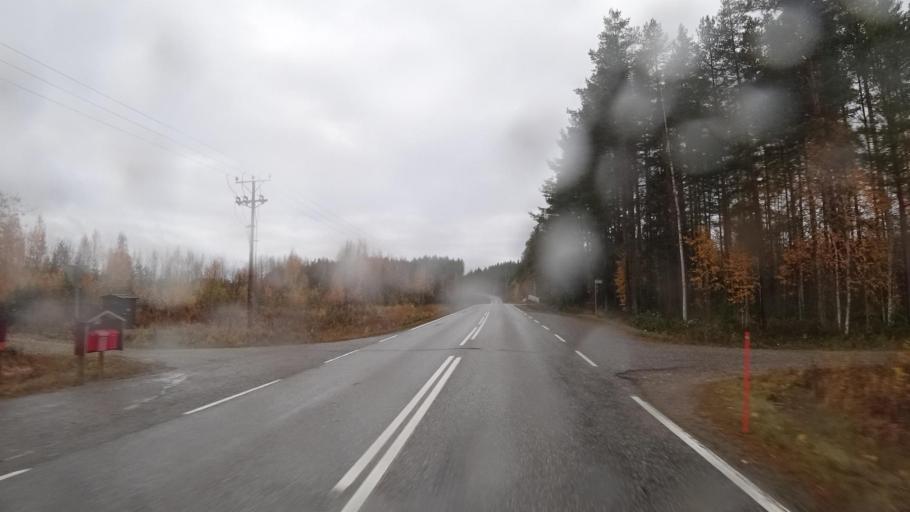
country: FI
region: North Karelia
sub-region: Joensuu
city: Outokumpu
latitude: 62.6200
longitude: 28.9302
